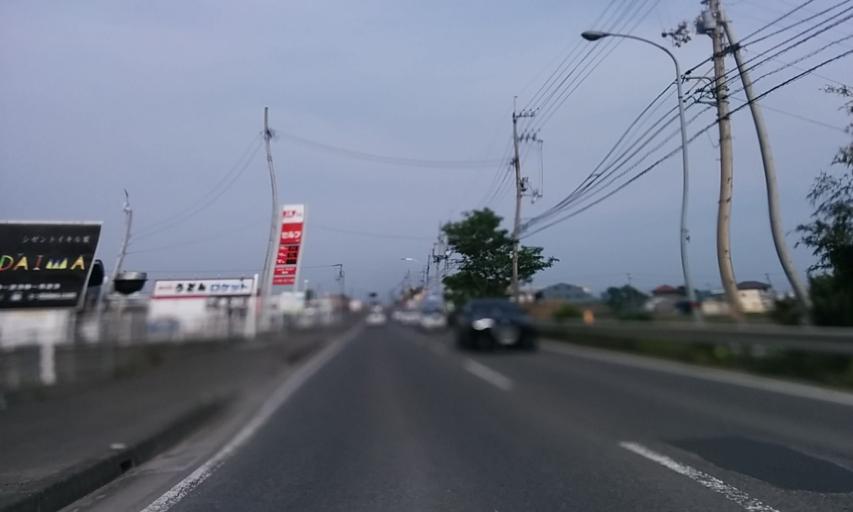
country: JP
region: Ehime
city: Kawanoecho
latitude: 33.9668
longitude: 133.4880
